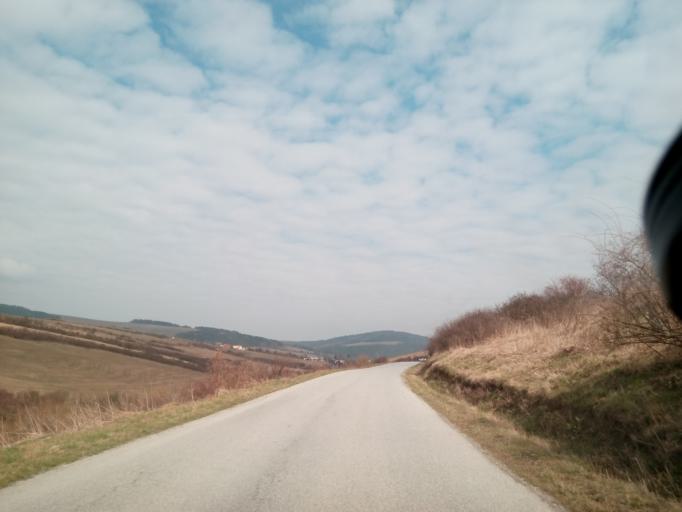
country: SK
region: Presovsky
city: Sabinov
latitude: 49.0317
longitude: 21.0188
